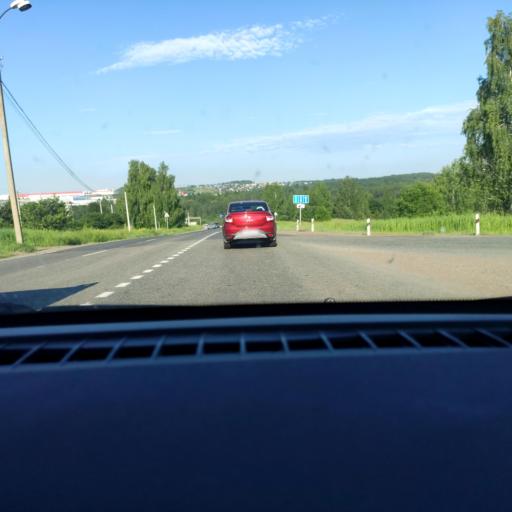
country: RU
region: Udmurtiya
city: Khokhryaki
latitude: 56.9141
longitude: 53.3944
